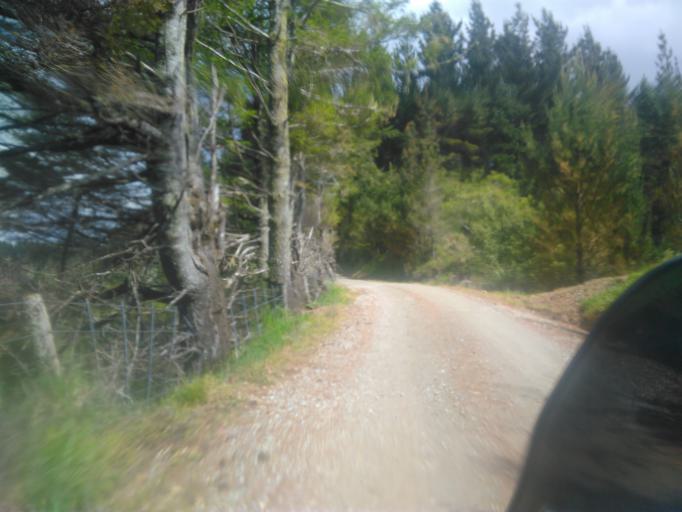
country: NZ
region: Hawke's Bay
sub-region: Wairoa District
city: Wairoa
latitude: -38.7699
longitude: 177.6033
